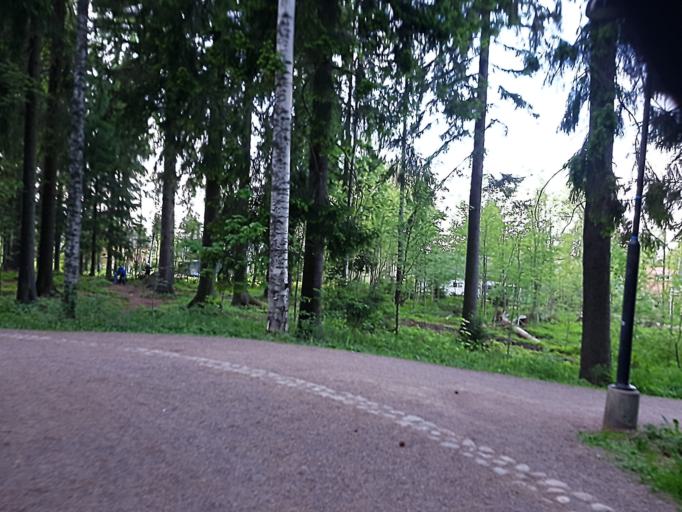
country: FI
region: Uusimaa
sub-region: Helsinki
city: Helsinki
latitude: 60.2356
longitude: 24.9384
